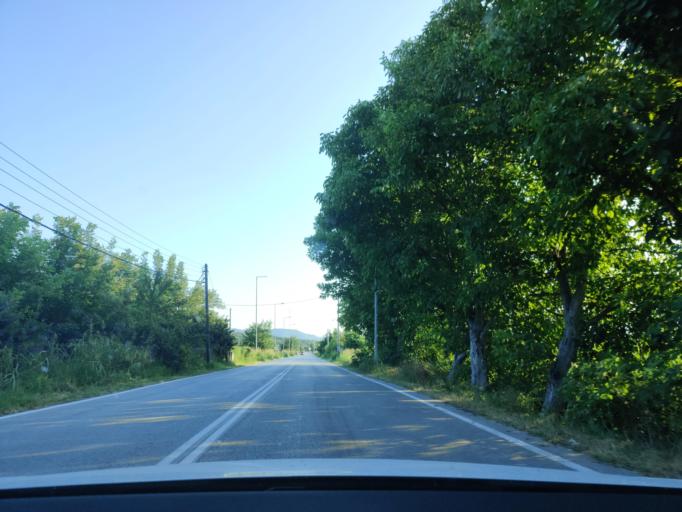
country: GR
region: East Macedonia and Thrace
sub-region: Nomos Kavalas
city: Amygdaleonas
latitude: 40.9816
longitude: 24.3683
